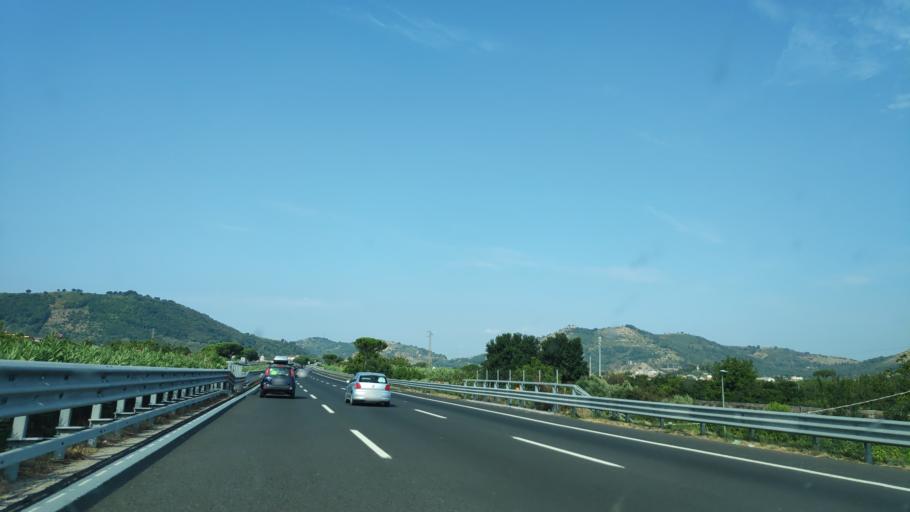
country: IT
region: Campania
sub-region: Provincia di Salerno
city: Roccapiemonte
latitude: 40.7673
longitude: 14.6905
